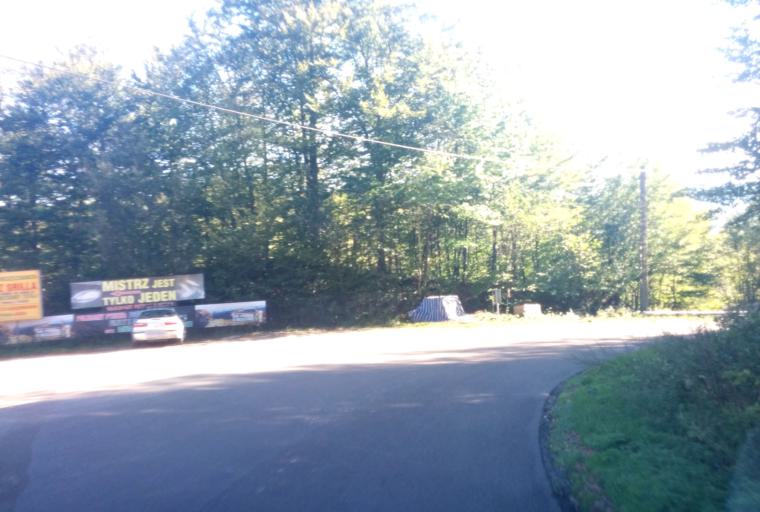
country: PL
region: Subcarpathian Voivodeship
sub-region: Powiat leski
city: Polanczyk
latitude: 49.3019
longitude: 22.4326
